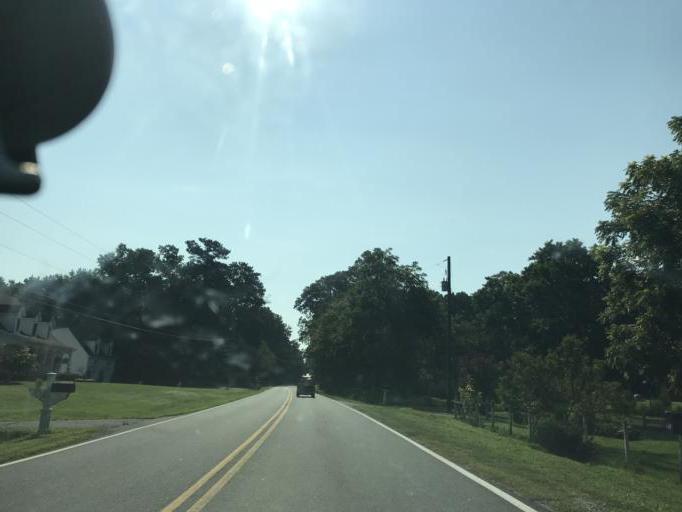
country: US
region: Georgia
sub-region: Forsyth County
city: Cumming
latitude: 34.2617
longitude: -84.1112
